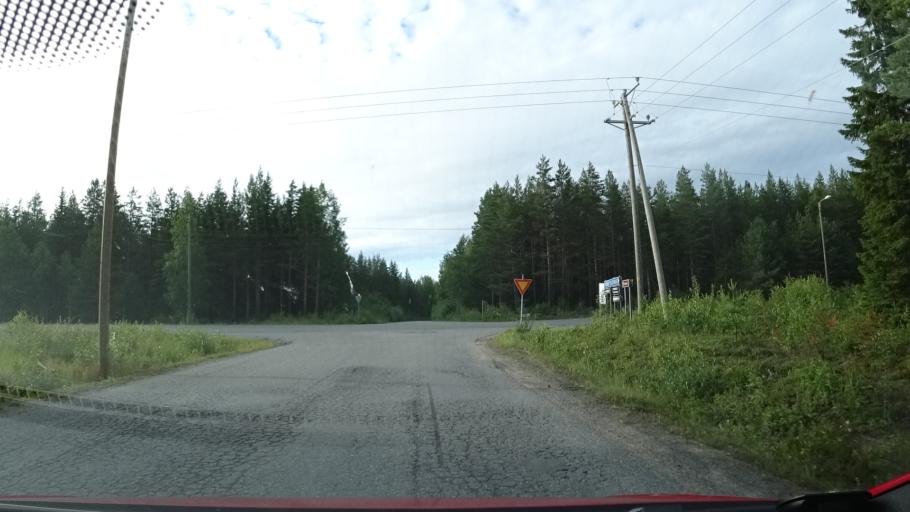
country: FI
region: Northern Ostrobothnia
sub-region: Oulu
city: Haukipudas
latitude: 65.2005
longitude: 25.4134
